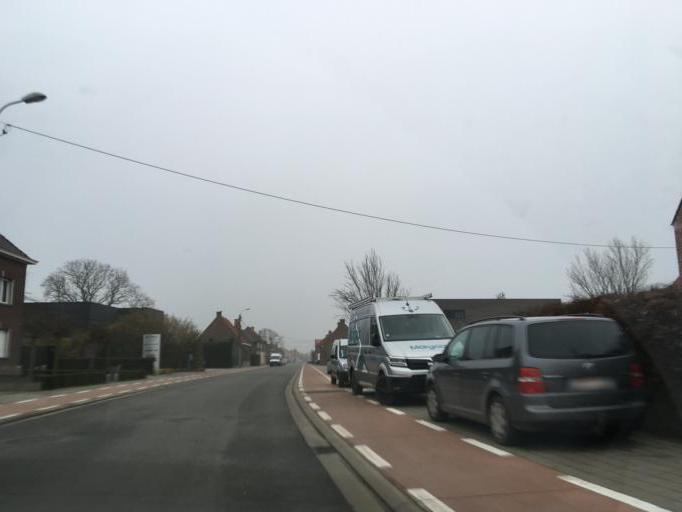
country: BE
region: Flanders
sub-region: Provincie West-Vlaanderen
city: Ardooie
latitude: 50.9906
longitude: 3.1665
